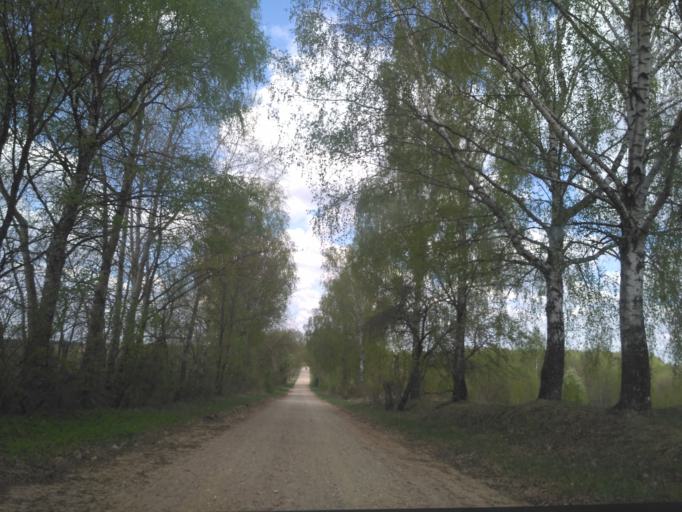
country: BY
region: Minsk
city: Il'ya
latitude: 54.2792
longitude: 27.3048
